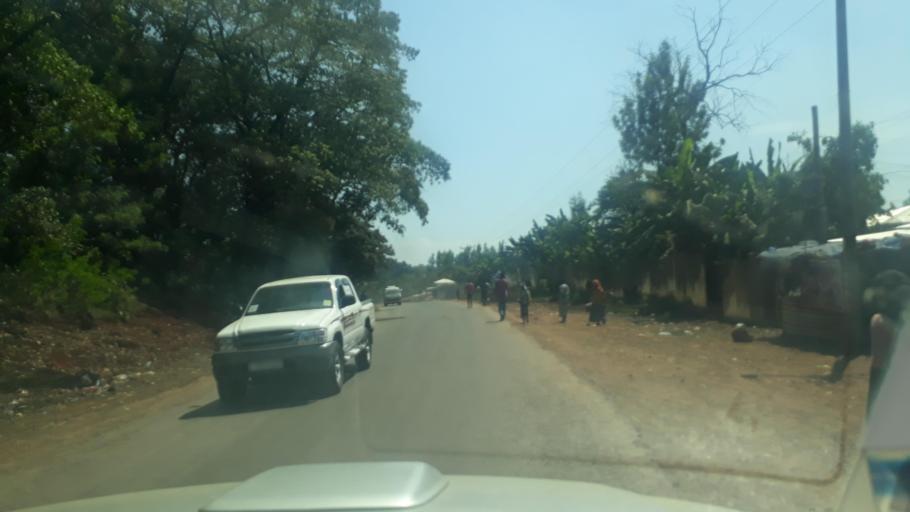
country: ET
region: Oromiya
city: Jima
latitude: 7.7023
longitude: 36.8066
